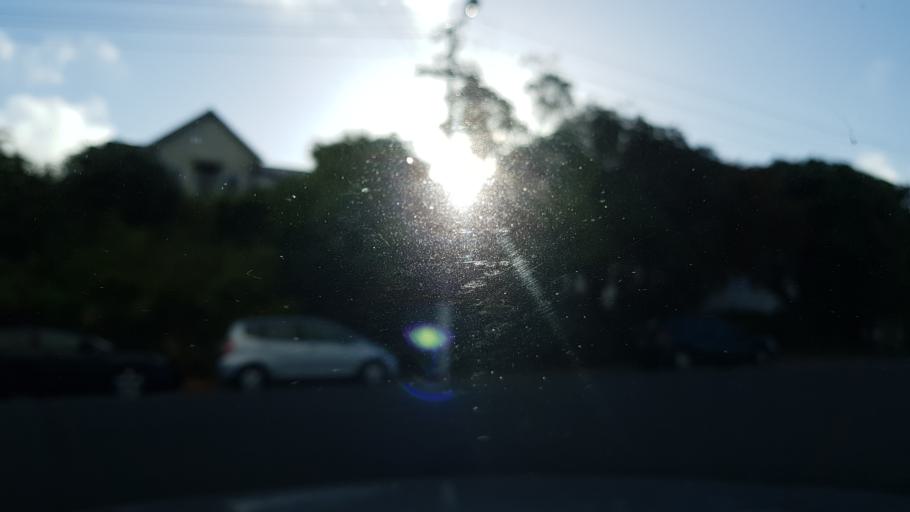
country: NZ
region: Auckland
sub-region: Auckland
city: North Shore
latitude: -36.8199
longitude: 174.7372
